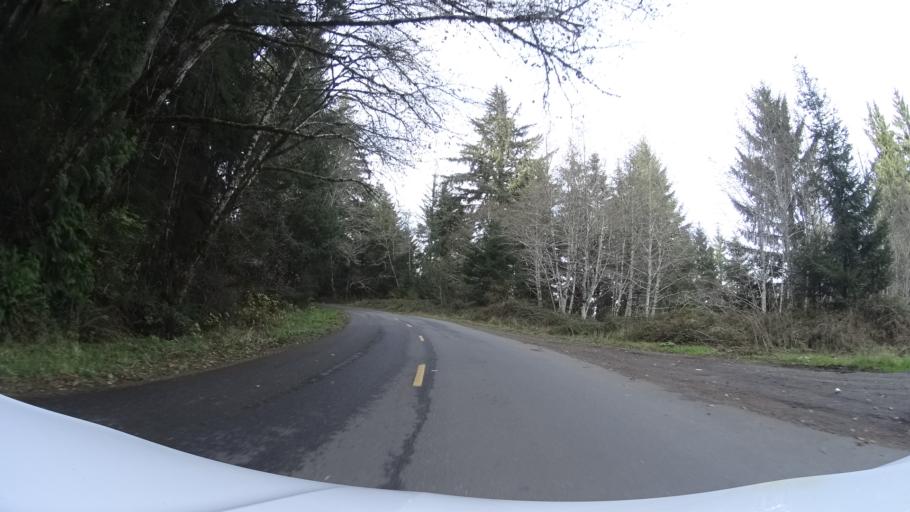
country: US
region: California
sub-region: Humboldt County
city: Ferndale
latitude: 40.5364
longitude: -124.2750
